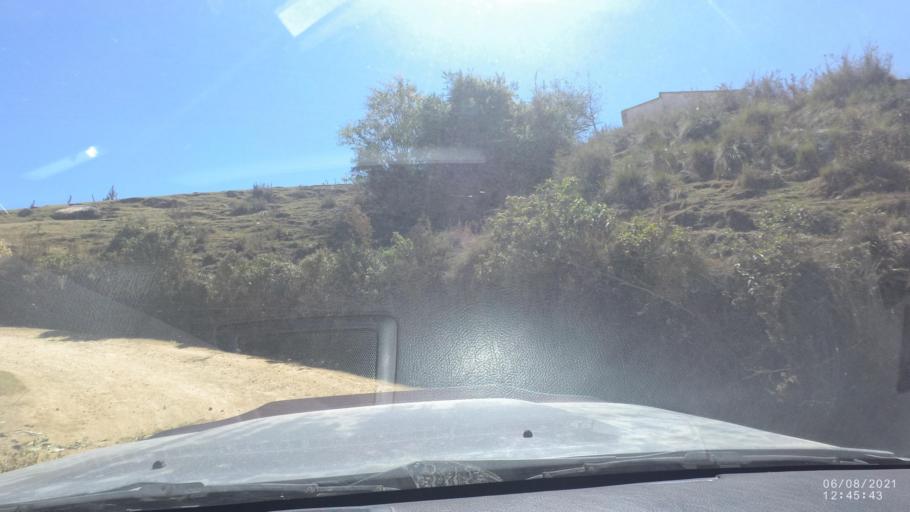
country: BO
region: Cochabamba
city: Colchani
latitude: -16.7640
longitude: -66.6649
